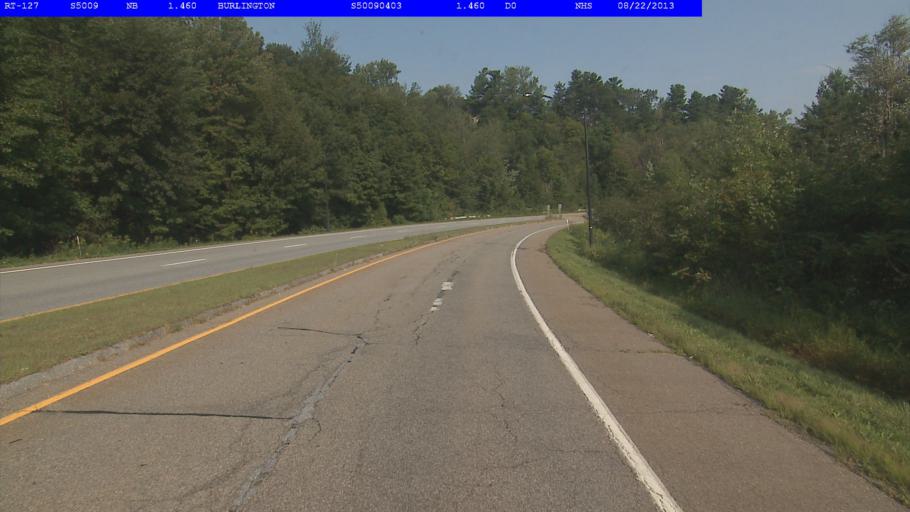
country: US
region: Vermont
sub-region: Chittenden County
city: Burlington
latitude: 44.5056
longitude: -73.2333
